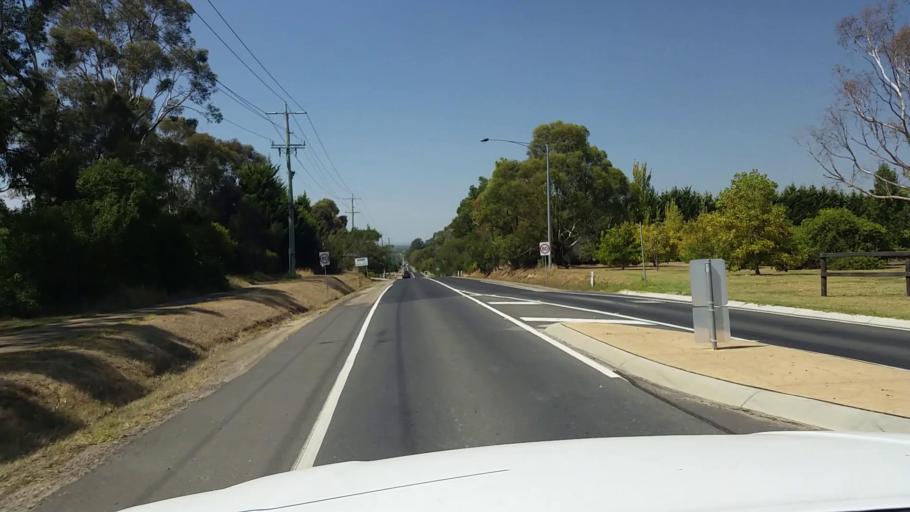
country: AU
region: Victoria
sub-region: Mornington Peninsula
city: Tyabb
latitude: -38.2385
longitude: 145.1727
